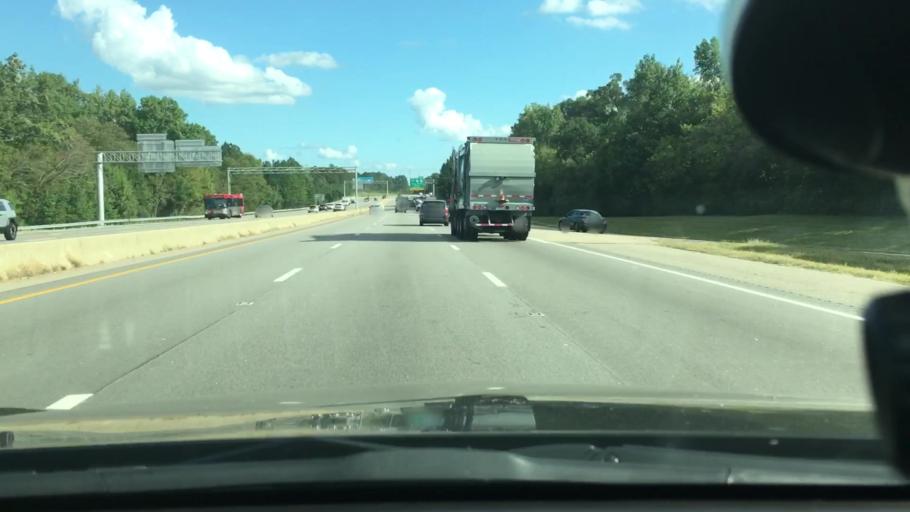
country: US
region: North Carolina
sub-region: Wake County
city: Raleigh
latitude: 35.7931
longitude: -78.5808
